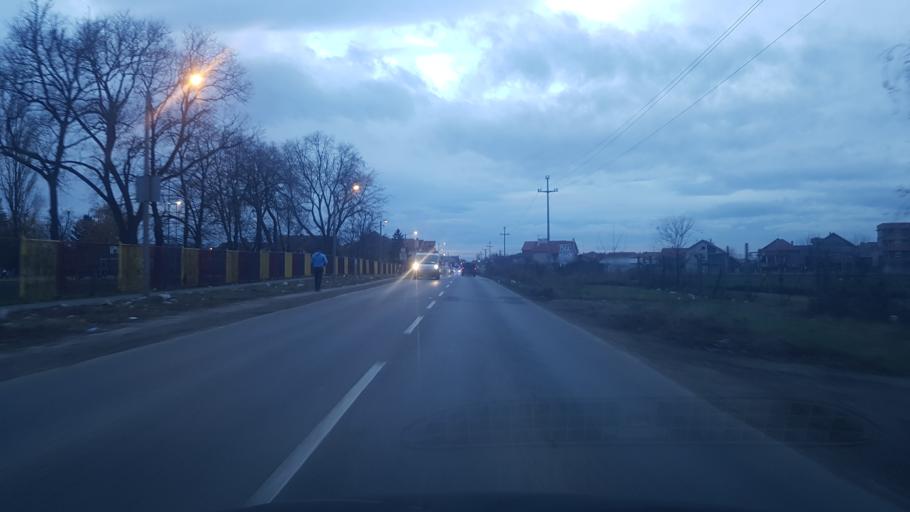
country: RS
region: Central Serbia
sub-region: Belgrade
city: Zemun
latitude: 44.8048
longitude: 20.3474
